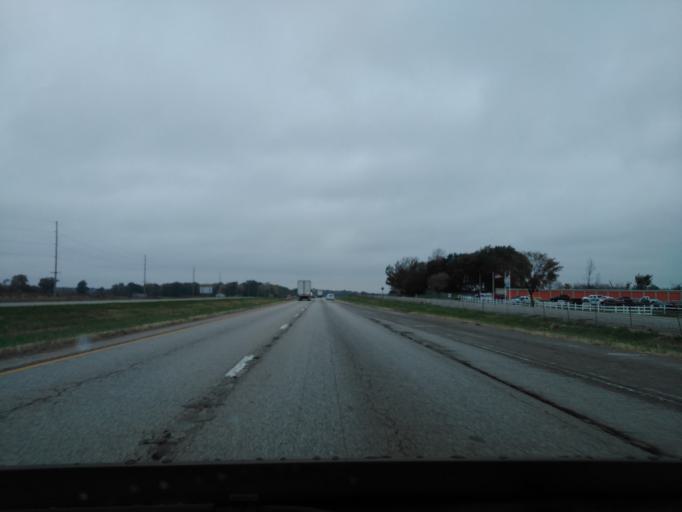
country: US
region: Illinois
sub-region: Bond County
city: Greenville
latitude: 38.8518
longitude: -89.4582
